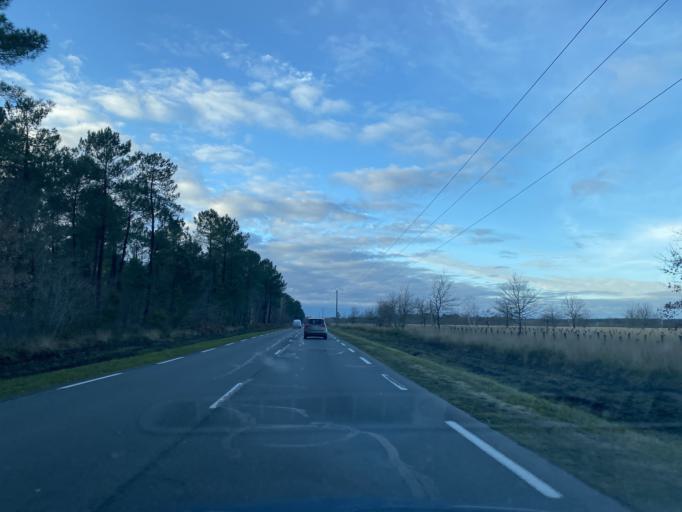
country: FR
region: Aquitaine
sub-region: Departement de la Gironde
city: Marcheprime
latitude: 44.7048
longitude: -0.8674
